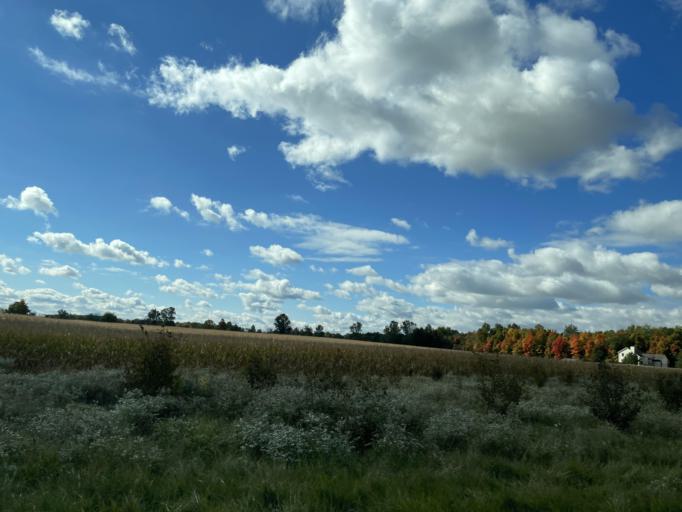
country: US
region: Indiana
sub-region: Allen County
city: Fort Wayne
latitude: 41.1140
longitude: -85.2282
